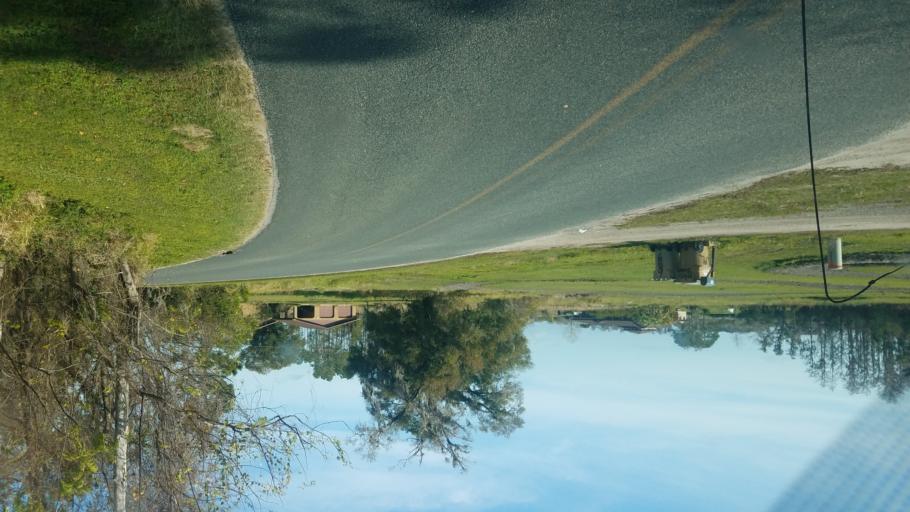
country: US
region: Florida
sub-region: Lake County
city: Clermont
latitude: 28.4446
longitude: -81.7917
